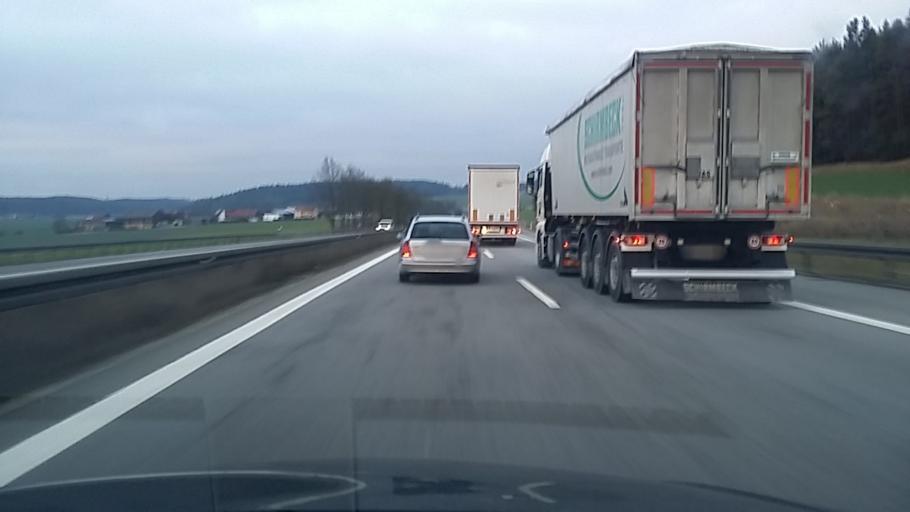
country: DE
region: Bavaria
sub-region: Upper Palatinate
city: Hohenfels
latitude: 49.1553
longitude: 11.8417
